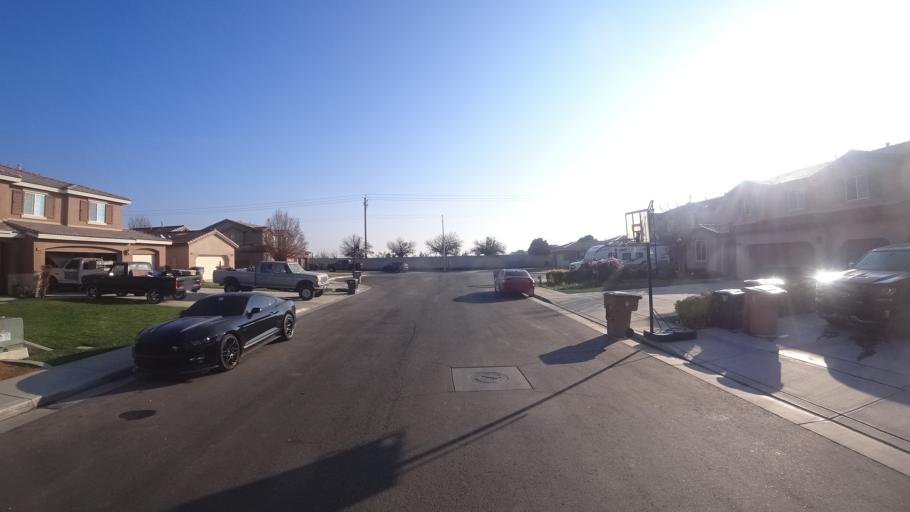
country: US
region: California
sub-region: Kern County
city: Greenacres
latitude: 35.2930
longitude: -119.1196
